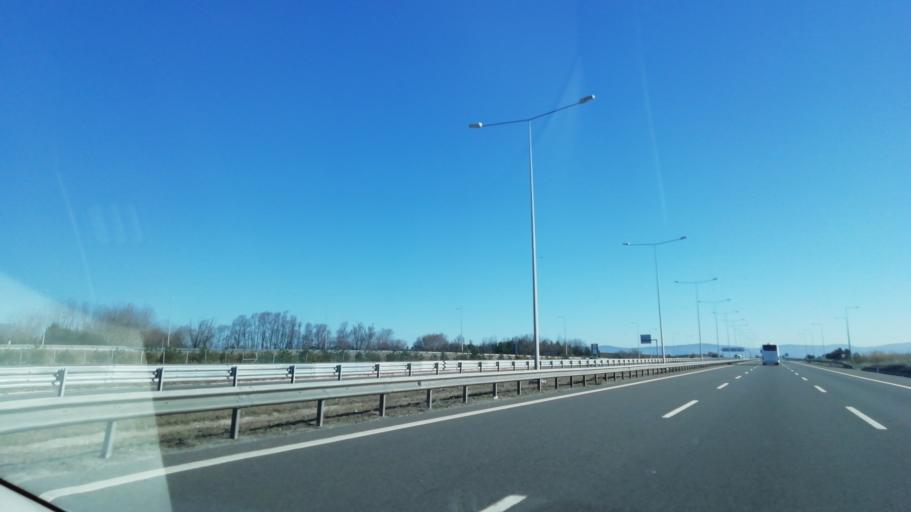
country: TR
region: Bolu
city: Dortdivan
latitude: 40.7428
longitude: 32.1218
